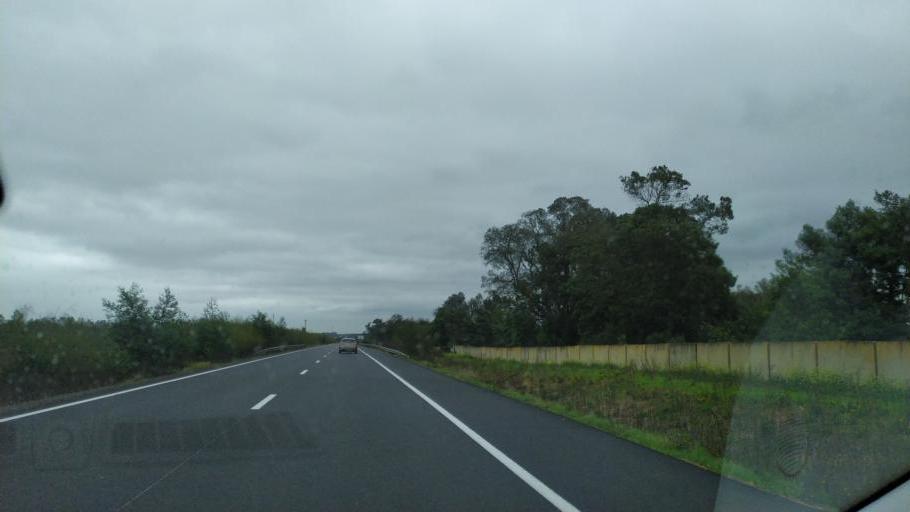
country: MA
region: Gharb-Chrarda-Beni Hssen
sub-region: Kenitra Province
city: Kenitra
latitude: 34.1838
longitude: -6.6470
